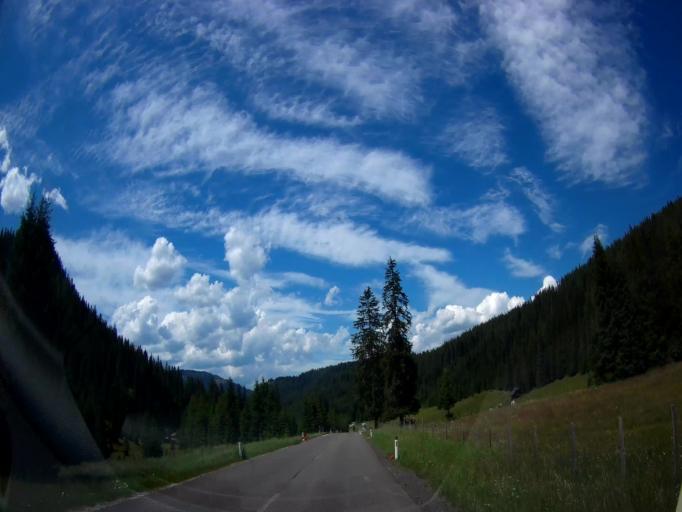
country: AT
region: Carinthia
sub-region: Politischer Bezirk Sankt Veit an der Glan
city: Glodnitz
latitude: 46.9553
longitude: 14.0250
